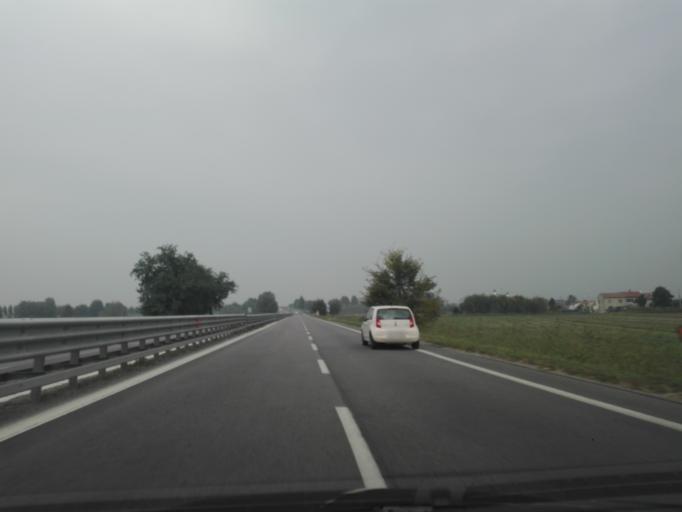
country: IT
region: Veneto
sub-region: Provincia di Verona
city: Legnago
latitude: 45.1713
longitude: 11.2922
